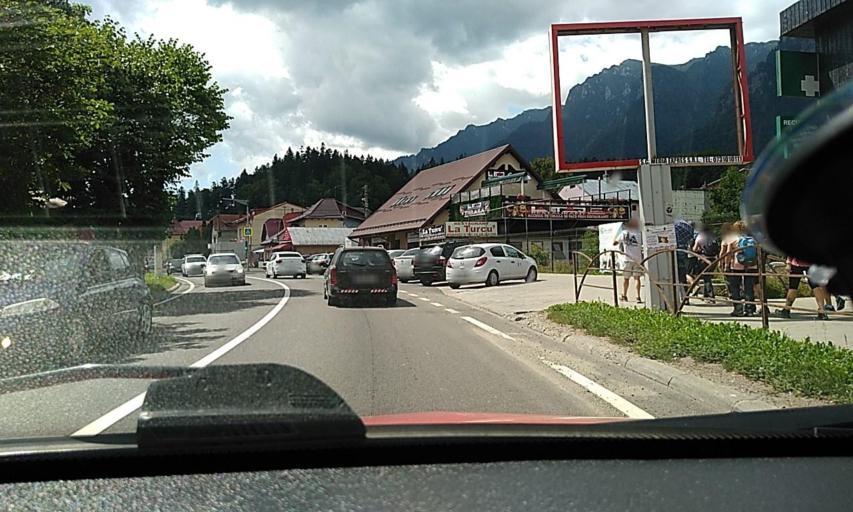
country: RO
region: Prahova
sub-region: Oras Busteni
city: Busteni
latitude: 45.4113
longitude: 25.5318
